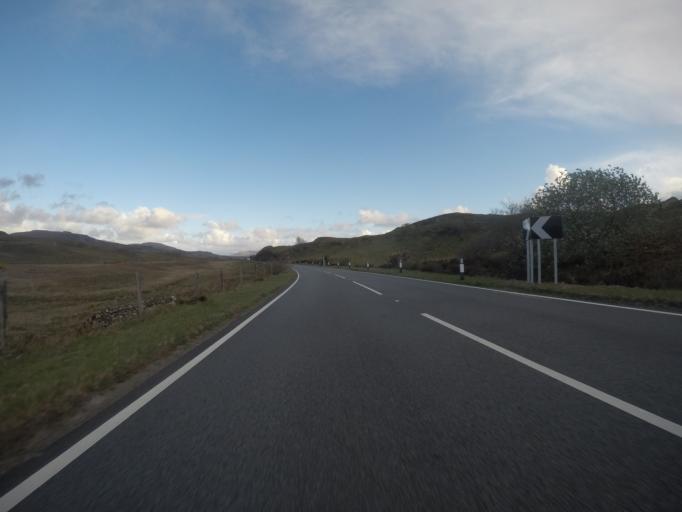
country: GB
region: Scotland
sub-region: Highland
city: Isle of Skye
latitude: 57.5110
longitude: -6.3402
